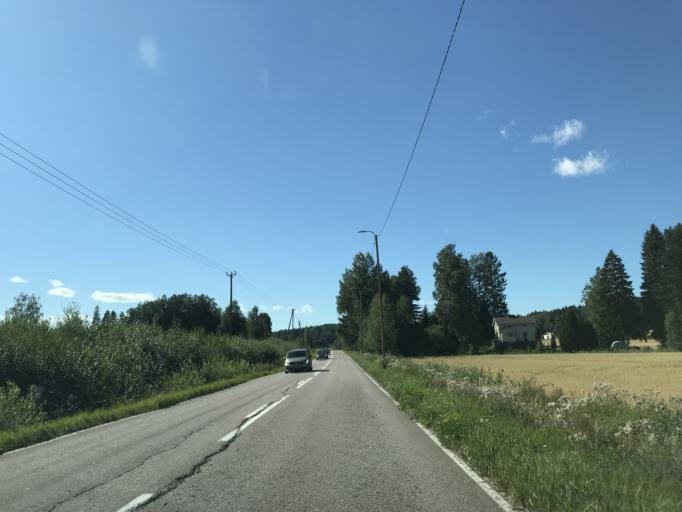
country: FI
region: Uusimaa
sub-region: Helsinki
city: Nurmijaervi
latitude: 60.4906
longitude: 24.6288
